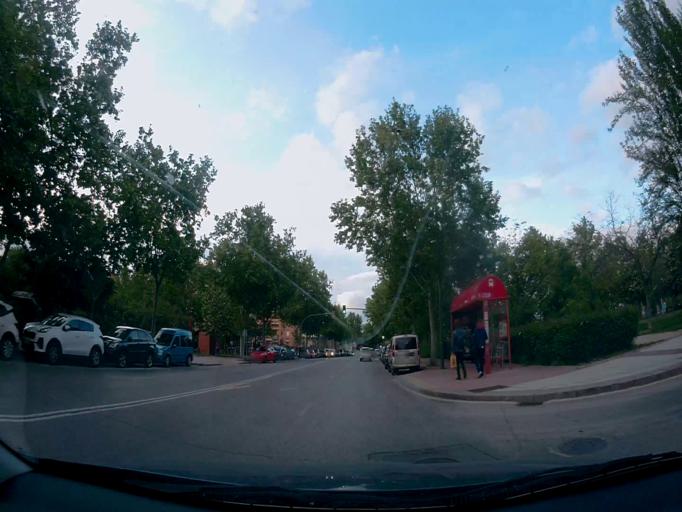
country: ES
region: Madrid
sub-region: Provincia de Madrid
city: Mostoles
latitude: 40.3270
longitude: -3.8826
